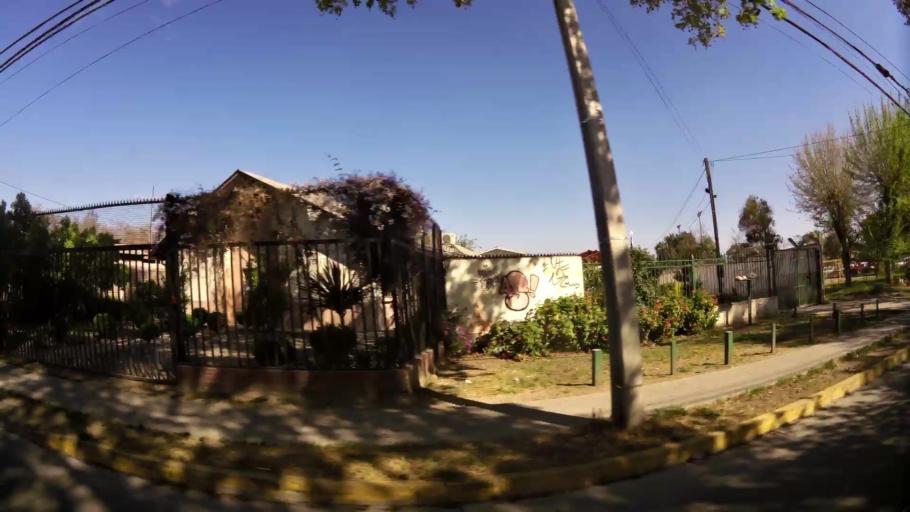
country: CL
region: Santiago Metropolitan
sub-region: Provincia de Talagante
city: Penaflor
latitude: -33.6063
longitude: -70.8944
